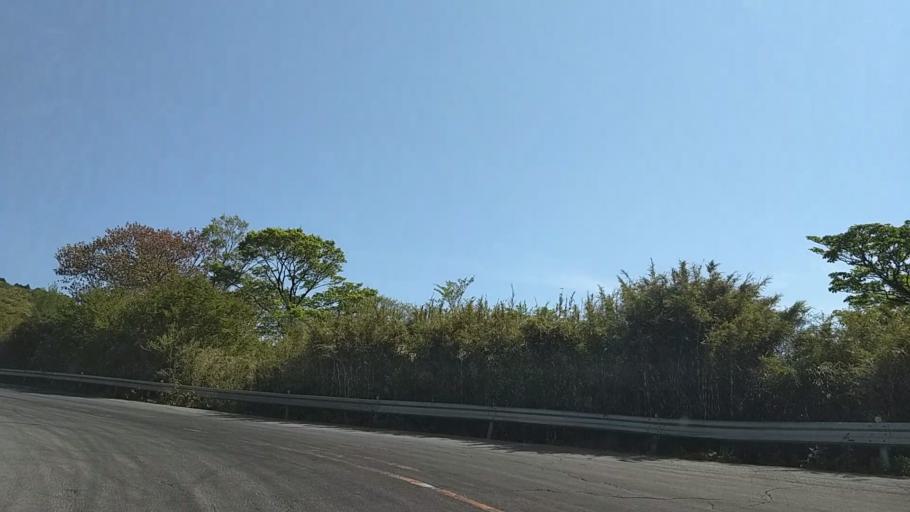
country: JP
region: Shizuoka
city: Gotemba
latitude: 35.2608
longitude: 138.9702
